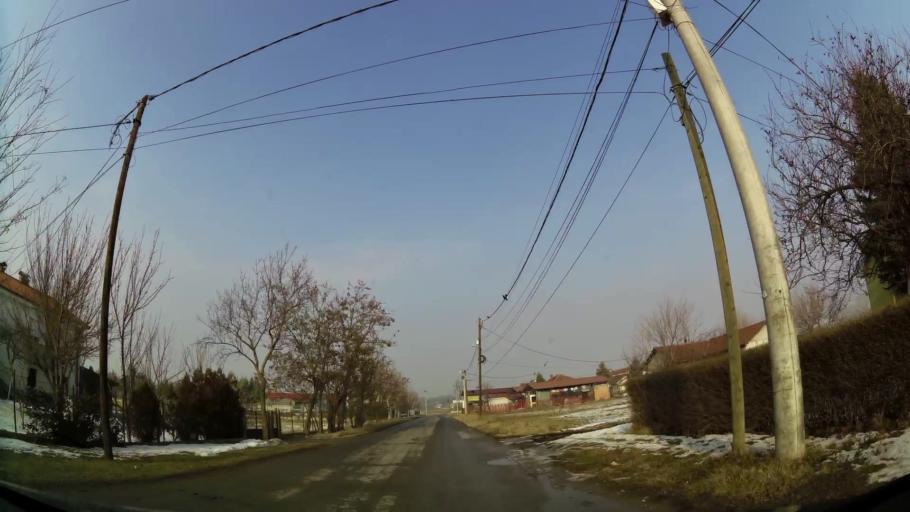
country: MK
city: Kadino
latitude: 41.9745
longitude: 21.5979
